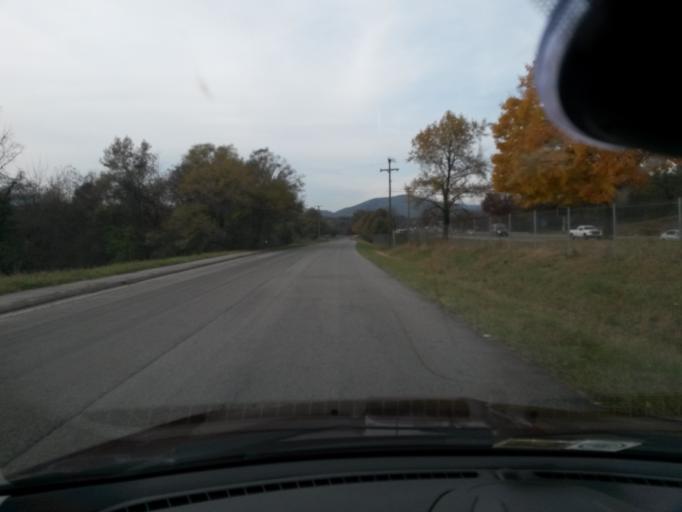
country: US
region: Virginia
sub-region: Roanoke County
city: Hollins
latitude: 37.3142
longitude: -79.9803
